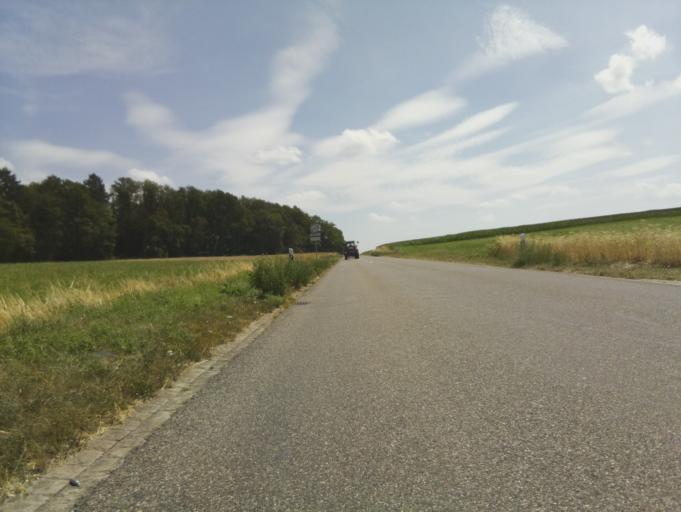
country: CH
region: Zurich
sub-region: Bezirk Andelfingen
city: Marthalen
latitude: 47.6334
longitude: 8.6597
